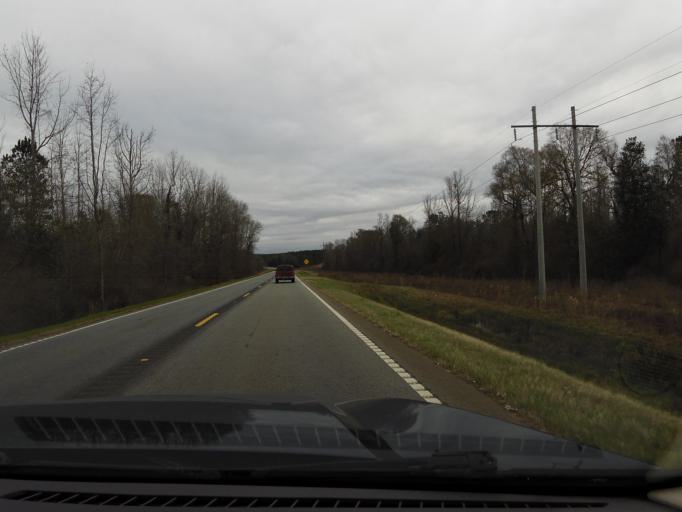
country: US
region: Georgia
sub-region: Randolph County
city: Shellman
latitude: 31.7731
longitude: -84.5657
